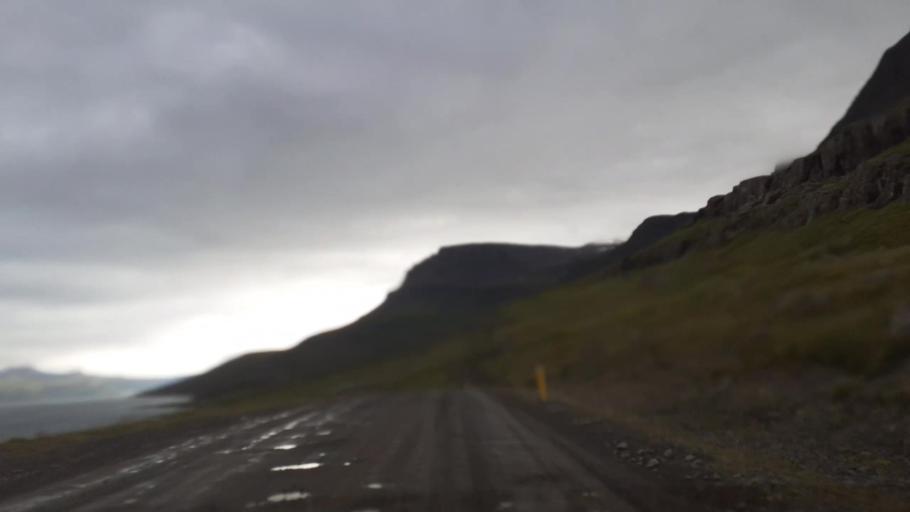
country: IS
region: East
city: Reydarfjoerdur
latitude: 65.0130
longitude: -14.1841
